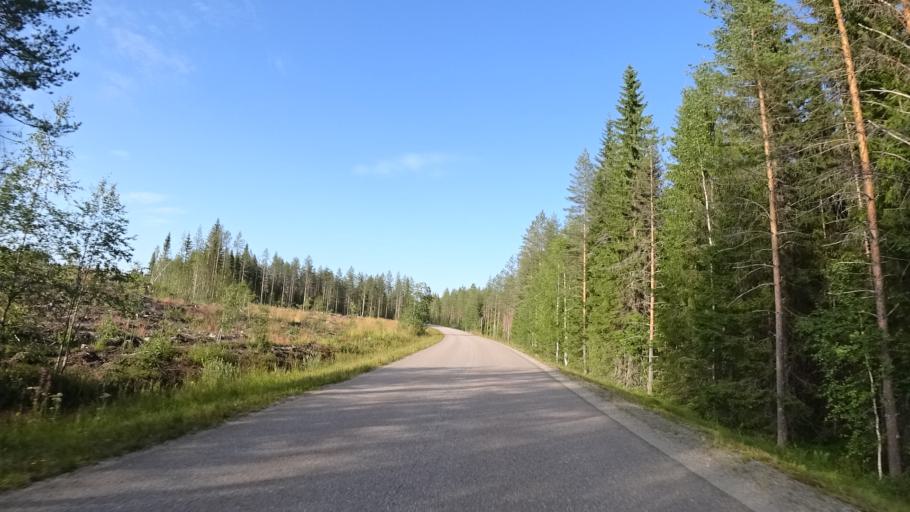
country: FI
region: North Karelia
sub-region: Joensuu
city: Eno
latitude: 63.0320
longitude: 30.5294
